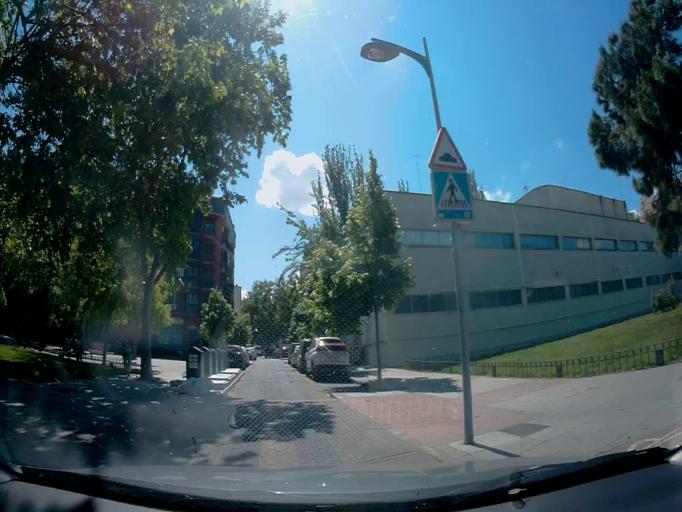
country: ES
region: Madrid
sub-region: Provincia de Madrid
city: Alcorcon
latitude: 40.3482
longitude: -3.8336
